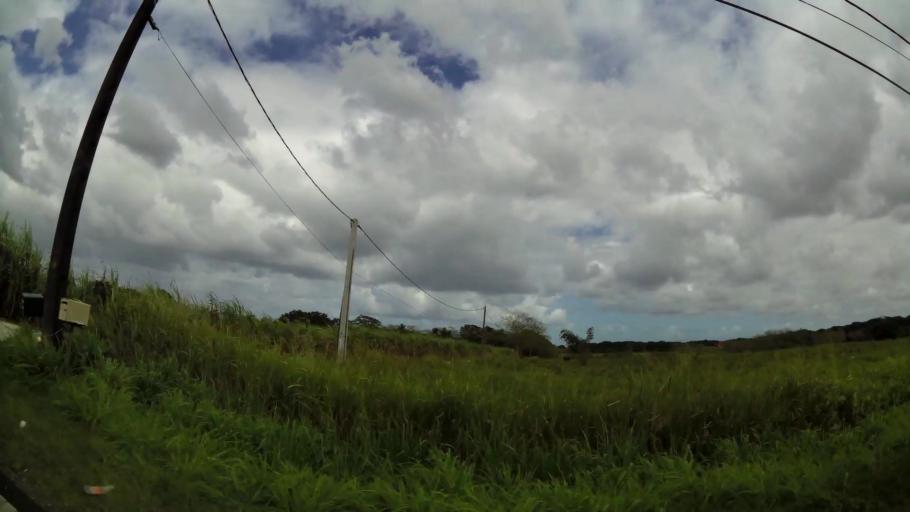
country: GP
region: Guadeloupe
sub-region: Guadeloupe
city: Lamentin
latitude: 16.2610
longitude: -61.6186
